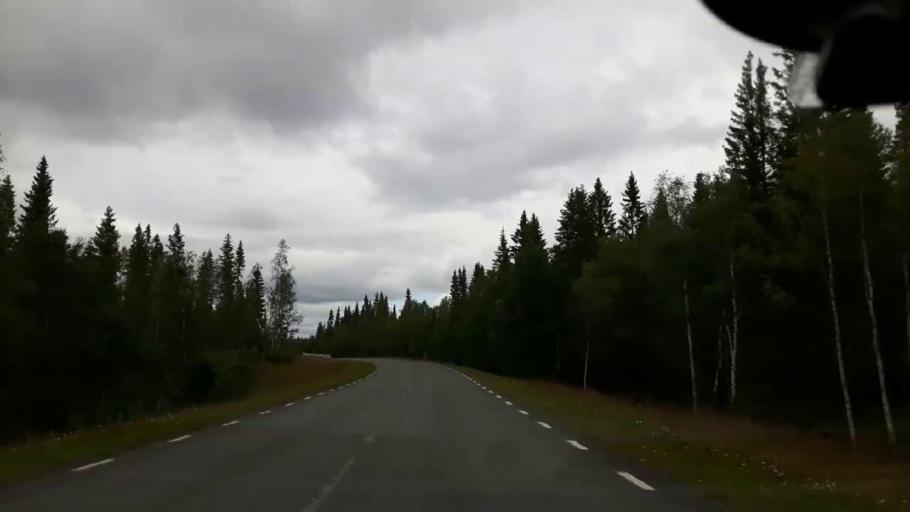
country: SE
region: Jaemtland
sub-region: Krokoms Kommun
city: Valla
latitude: 63.5456
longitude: 13.8530
